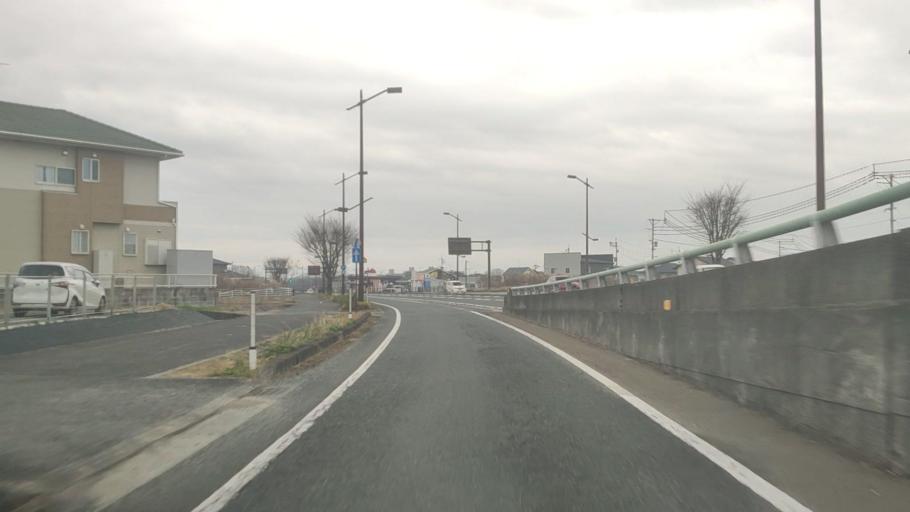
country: JP
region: Kumamoto
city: Ozu
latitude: 32.8248
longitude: 130.7913
